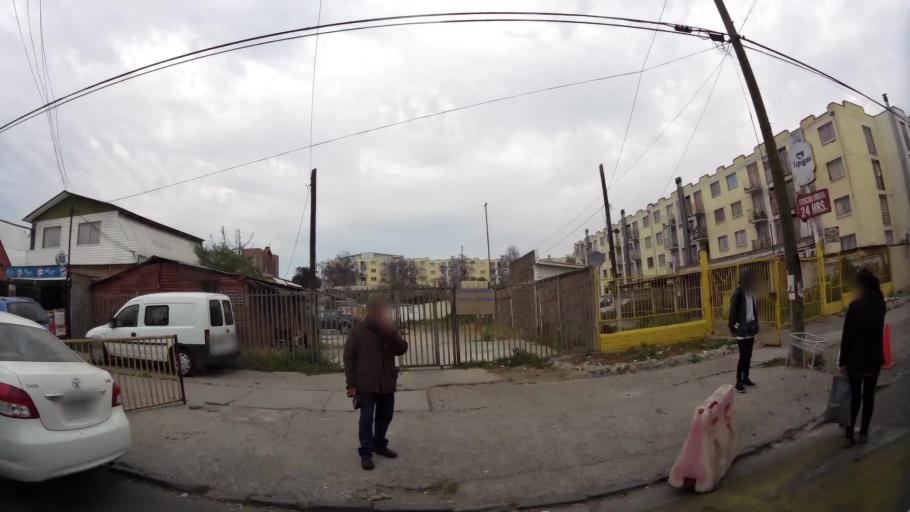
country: CL
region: Santiago Metropolitan
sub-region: Provincia de Santiago
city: Lo Prado
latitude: -33.5014
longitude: -70.7625
